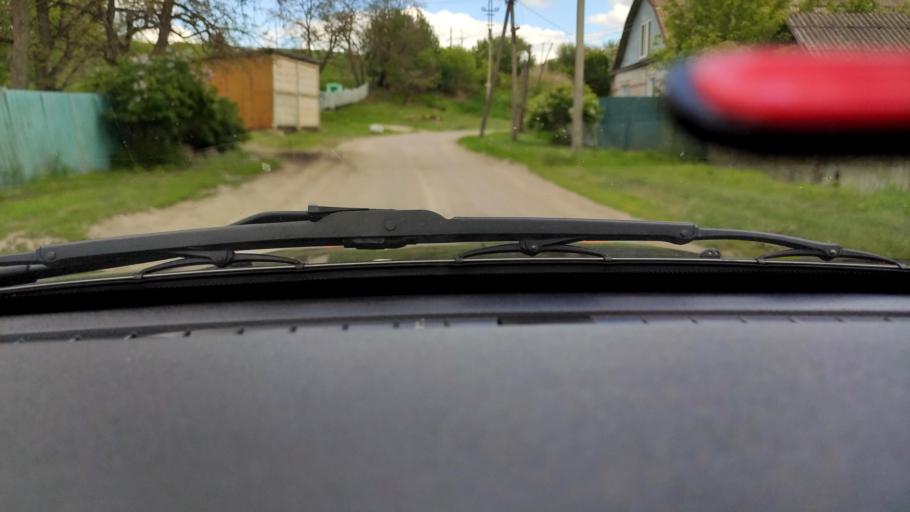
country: RU
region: Voronezj
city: Uryv-Pokrovka
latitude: 51.1106
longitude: 39.1629
